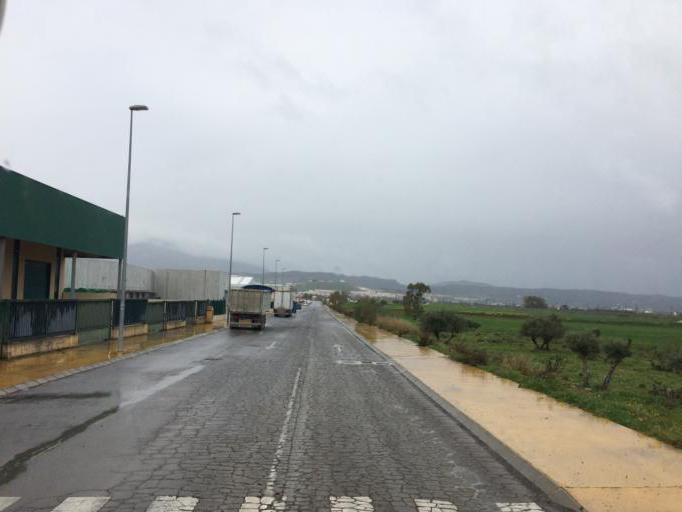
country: ES
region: Andalusia
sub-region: Provincia de Malaga
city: Antequera
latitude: 37.0452
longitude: -4.5216
